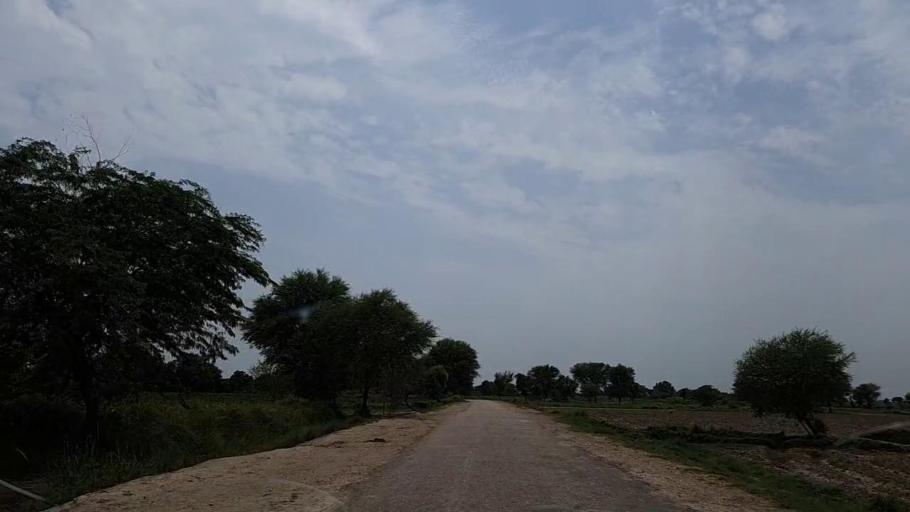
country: PK
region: Sindh
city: Tharu Shah
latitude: 26.9136
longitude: 68.0947
